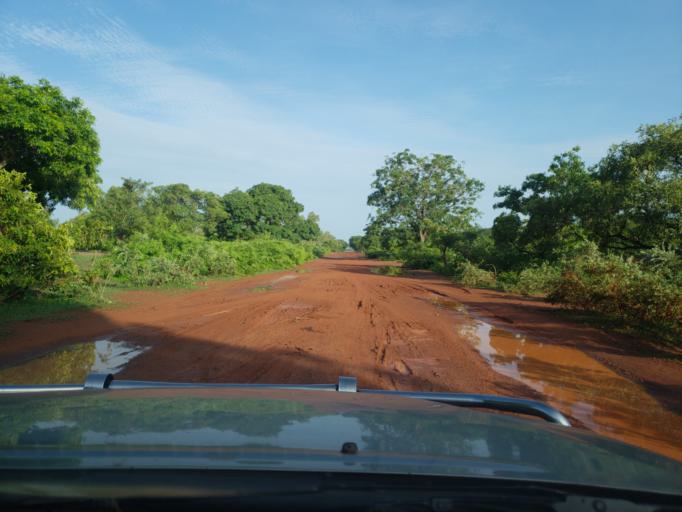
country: ML
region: Sikasso
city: Koutiala
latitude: 12.4265
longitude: -5.5980
